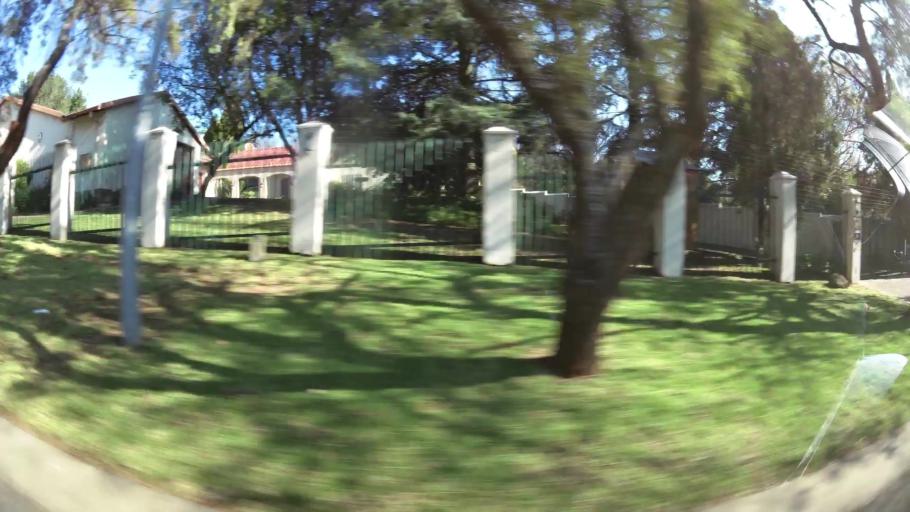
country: ZA
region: Gauteng
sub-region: City of Johannesburg Metropolitan Municipality
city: Midrand
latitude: -26.0681
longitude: 28.0488
